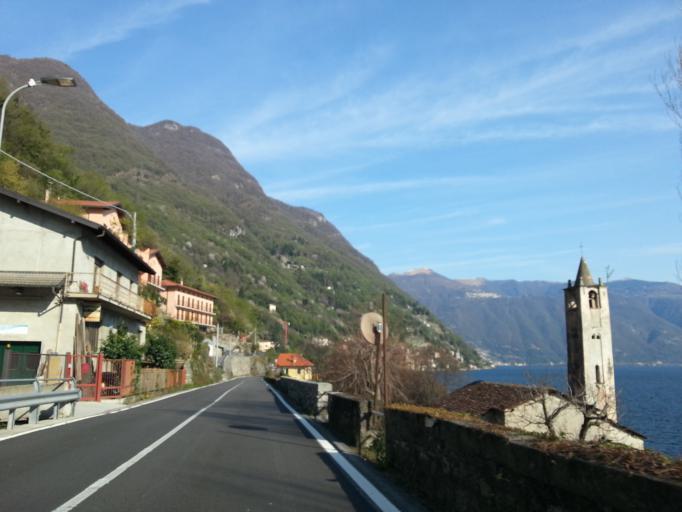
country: IT
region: Lombardy
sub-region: Provincia di Como
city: Brienno
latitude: 45.9019
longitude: 9.1353
